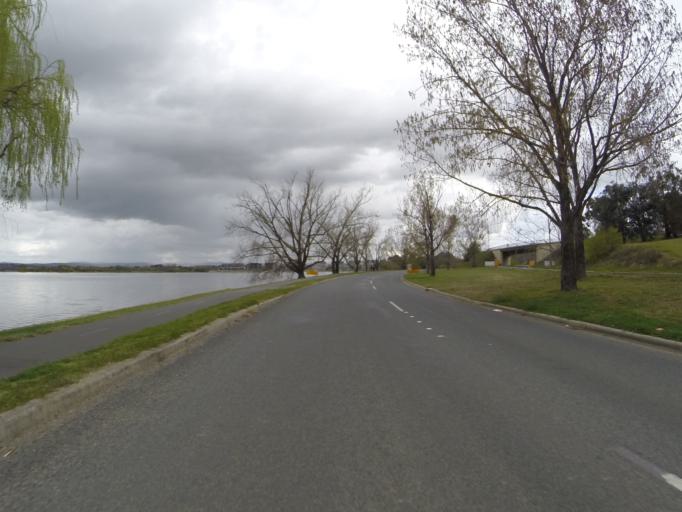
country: AU
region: Australian Capital Territory
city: Forrest
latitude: -35.3029
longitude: 149.1401
